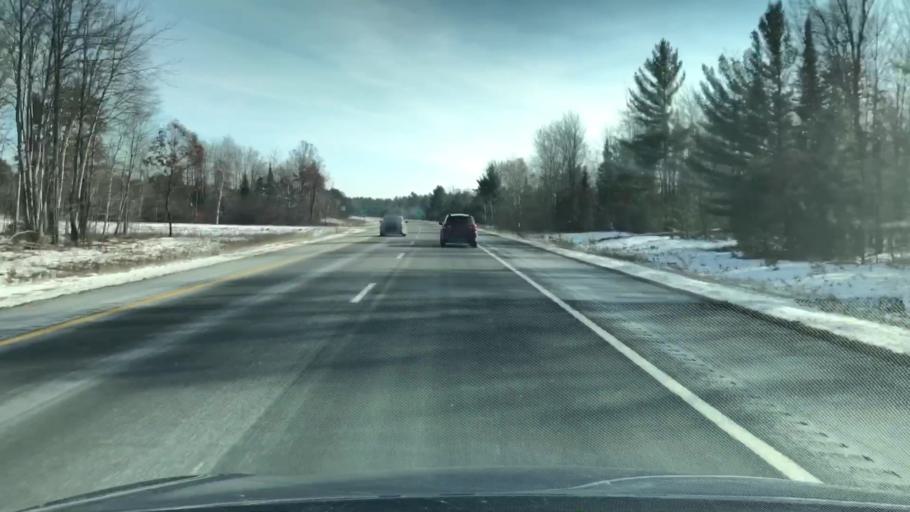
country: US
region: Michigan
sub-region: Roscommon County
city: Saint Helen
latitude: 44.3177
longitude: -84.5202
